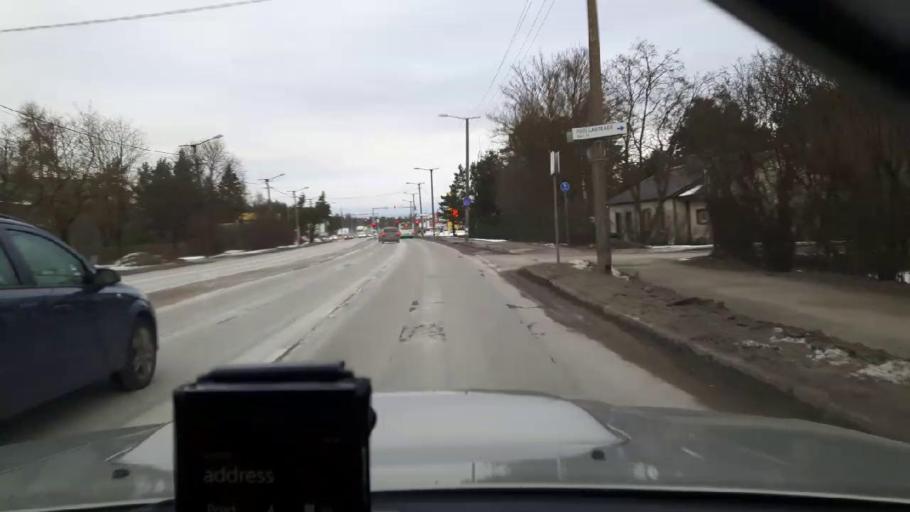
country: EE
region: Harju
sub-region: Saue vald
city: Laagri
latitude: 59.3570
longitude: 24.6310
